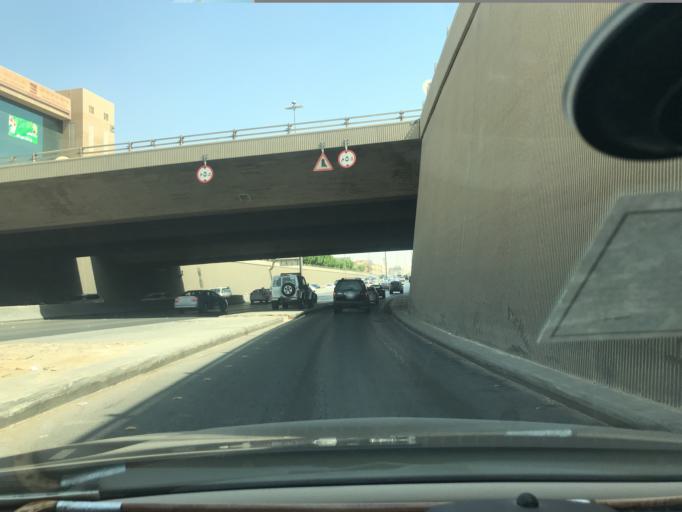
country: SA
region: Ar Riyad
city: Riyadh
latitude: 24.6798
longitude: 46.6915
